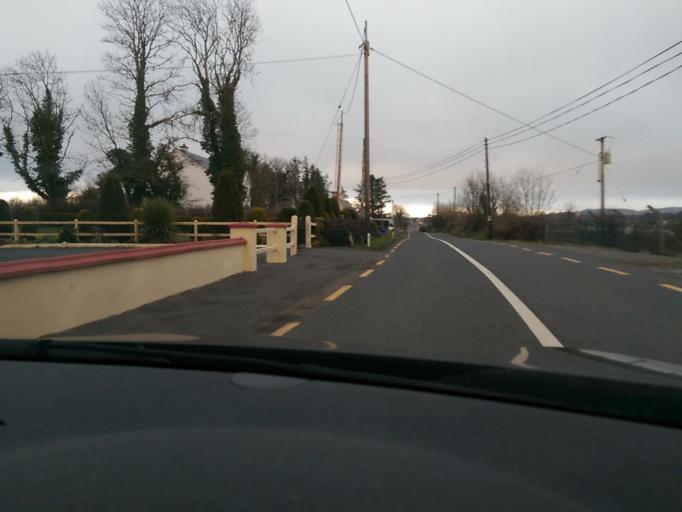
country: IE
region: Connaught
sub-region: Sligo
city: Ballymote
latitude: 54.0005
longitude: -8.5345
